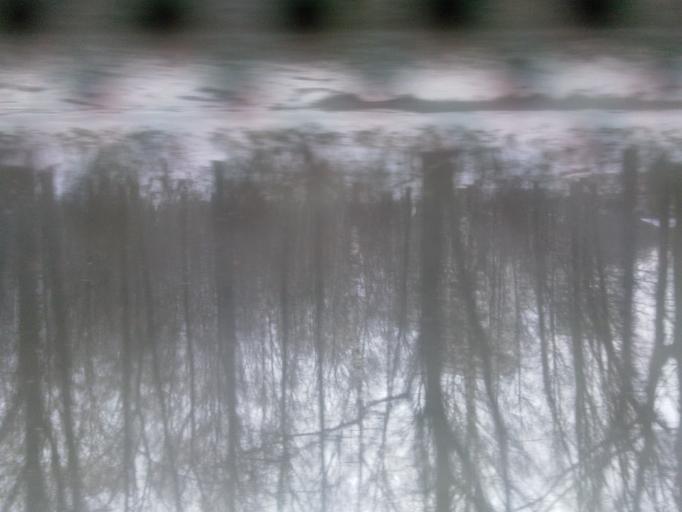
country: RU
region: Moscow
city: Troparevo
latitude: 55.6579
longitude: 37.5000
